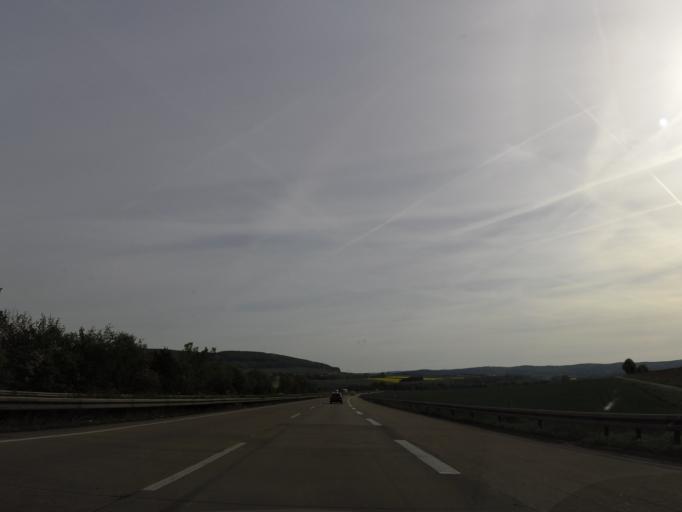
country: DE
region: Lower Saxony
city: Kalefeld
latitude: 51.7824
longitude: 10.0362
